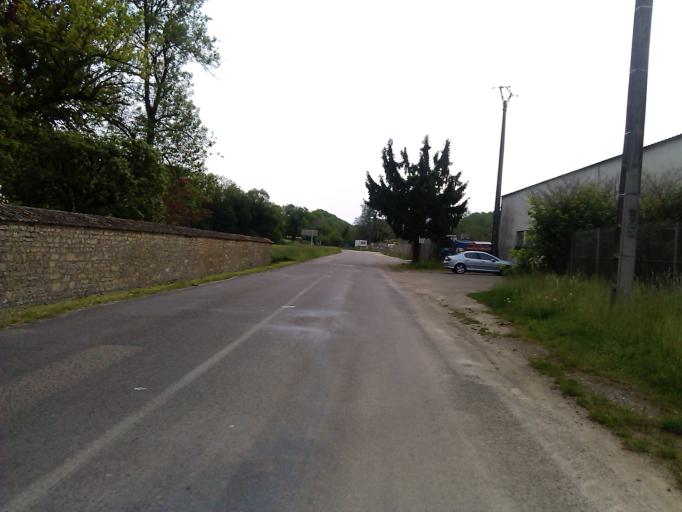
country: FR
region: Franche-Comte
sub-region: Departement du Jura
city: Dampierre
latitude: 47.1435
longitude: 5.7247
